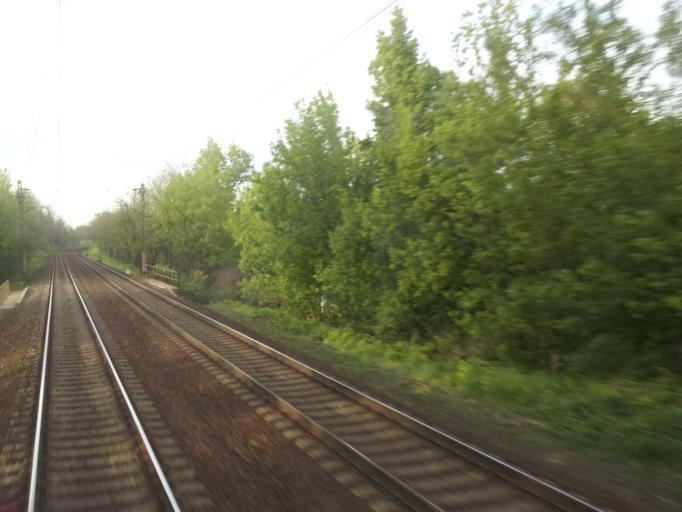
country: HU
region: Budapest
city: Budapest XV. keruelet
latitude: 47.5926
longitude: 19.1218
